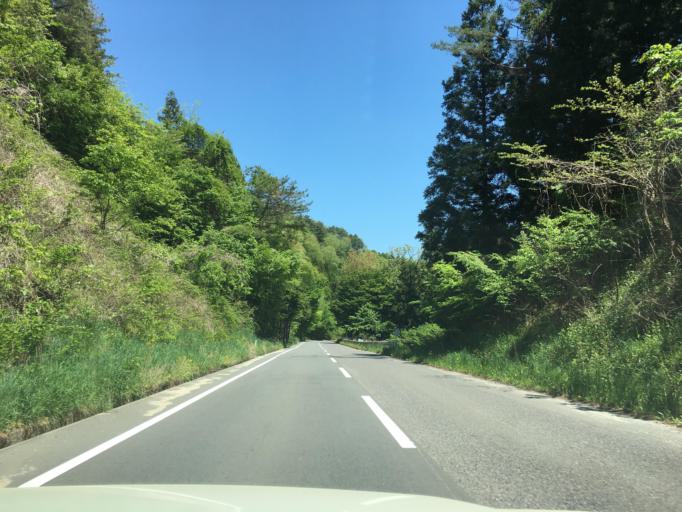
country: JP
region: Fukushima
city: Funehikimachi-funehiki
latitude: 37.3794
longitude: 140.6170
